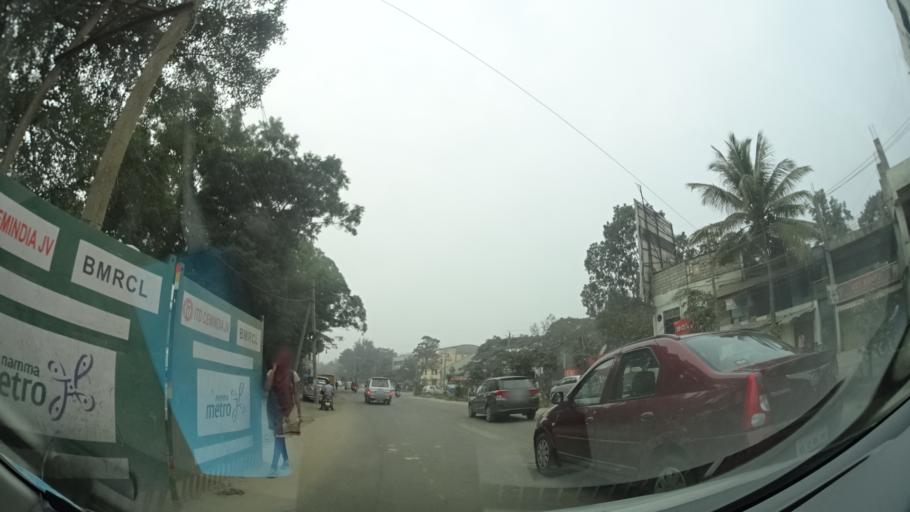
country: IN
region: Karnataka
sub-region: Bangalore Urban
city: Bangalore
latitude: 12.9857
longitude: 77.7084
